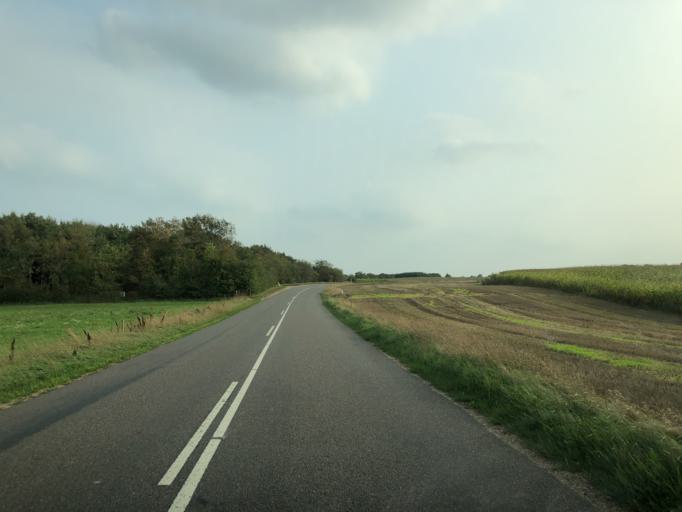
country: DK
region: Central Jutland
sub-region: Ringkobing-Skjern Kommune
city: Videbaek
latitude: 56.0792
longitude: 8.7051
